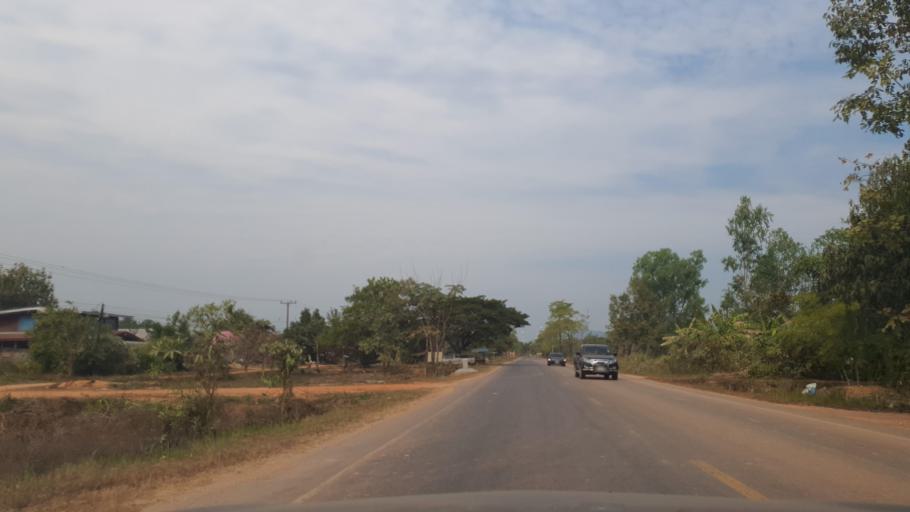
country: TH
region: Changwat Bueng Kan
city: Bung Khla
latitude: 18.1963
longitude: 104.0531
